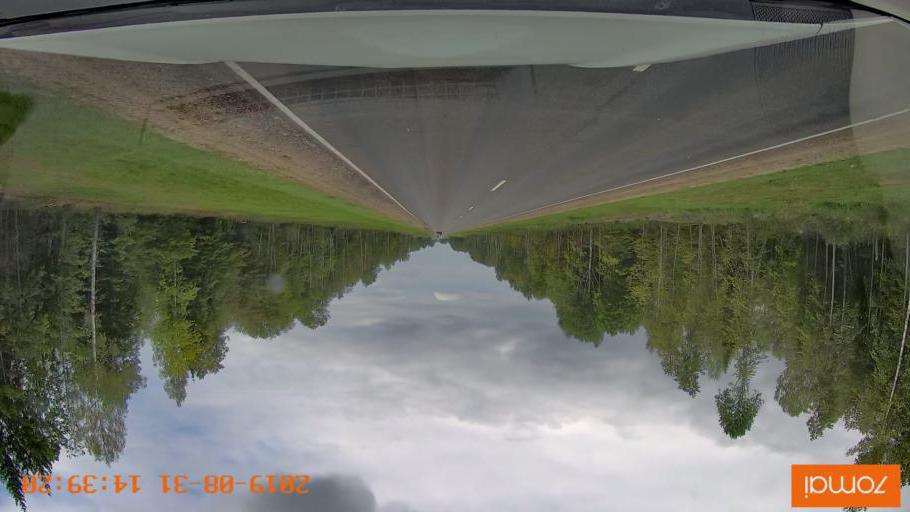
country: RU
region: Smolensk
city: Yekimovichi
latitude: 54.1908
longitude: 33.5499
